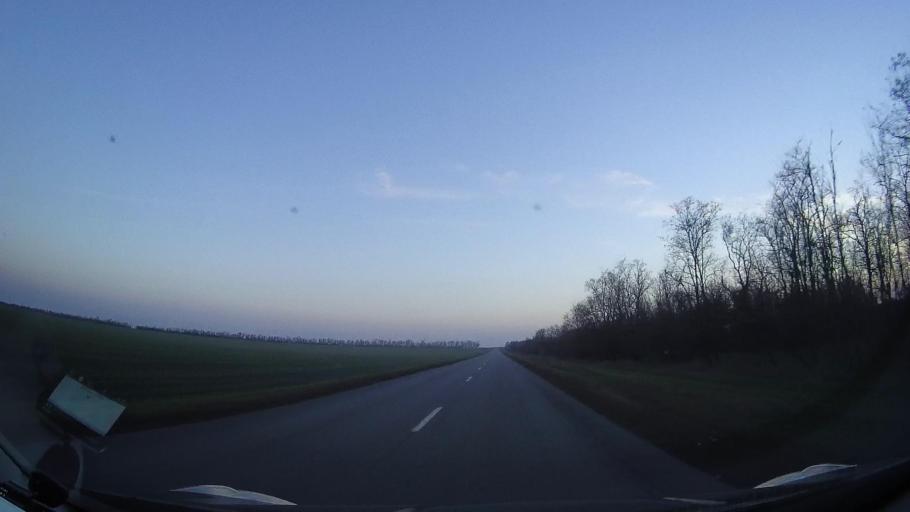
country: RU
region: Rostov
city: Zernograd
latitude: 46.9190
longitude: 40.3388
